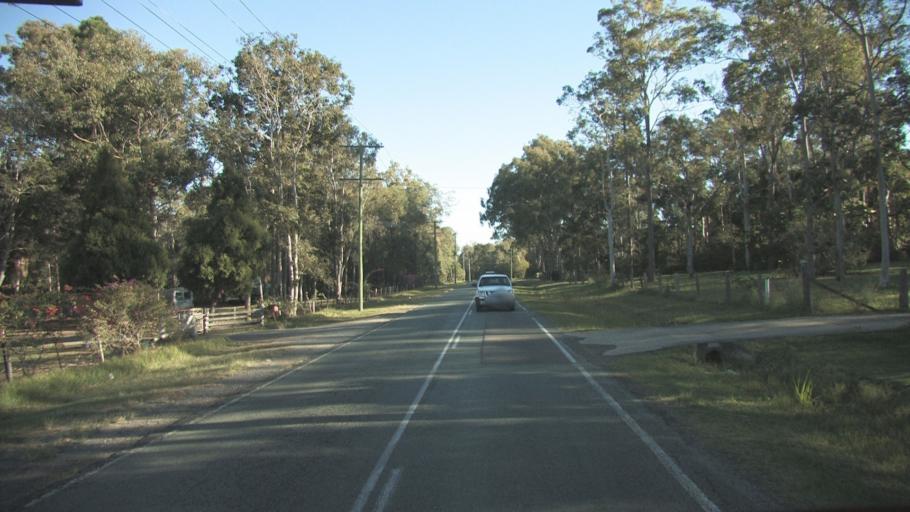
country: AU
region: Queensland
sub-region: Logan
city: Chambers Flat
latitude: -27.7532
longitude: 153.0519
